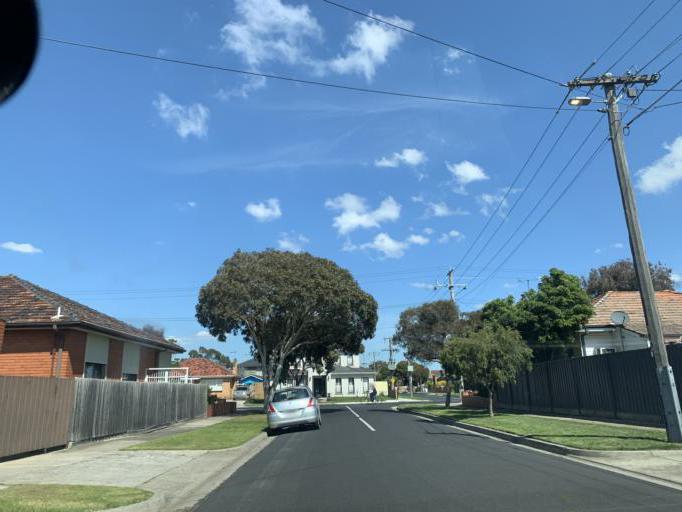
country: AU
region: Victoria
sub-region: Moreland
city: Pascoe Vale South
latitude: -37.7355
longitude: 144.9482
